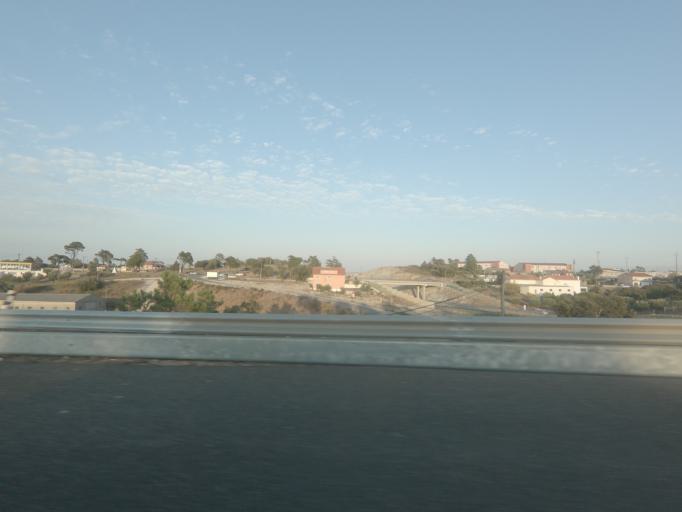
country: PT
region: Leiria
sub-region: Leiria
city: Santa Catarina da Serra
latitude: 39.6701
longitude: -8.6861
